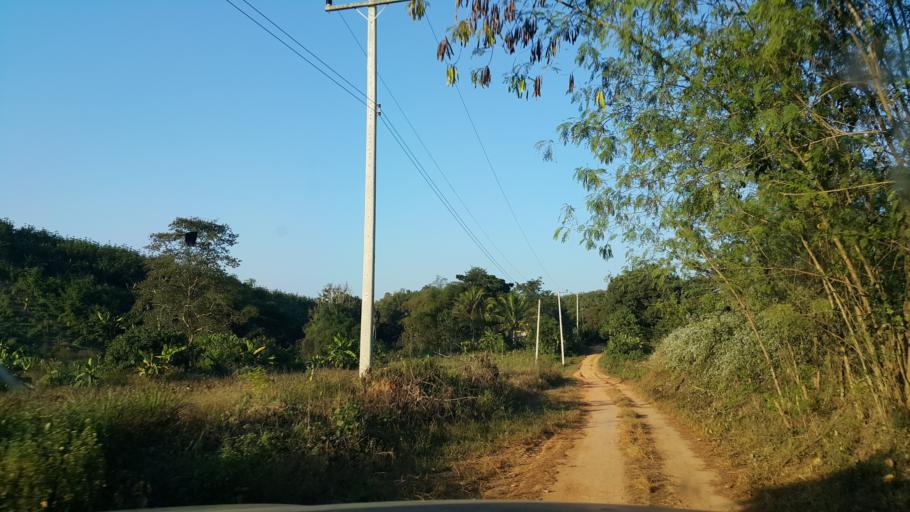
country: TH
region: Sukhothai
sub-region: Amphoe Si Satchanalai
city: Si Satchanalai
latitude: 17.5902
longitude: 99.6152
